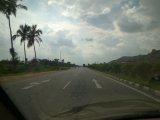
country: IN
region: Karnataka
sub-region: Kolar
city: Kolar
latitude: 13.1225
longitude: 78.0666
